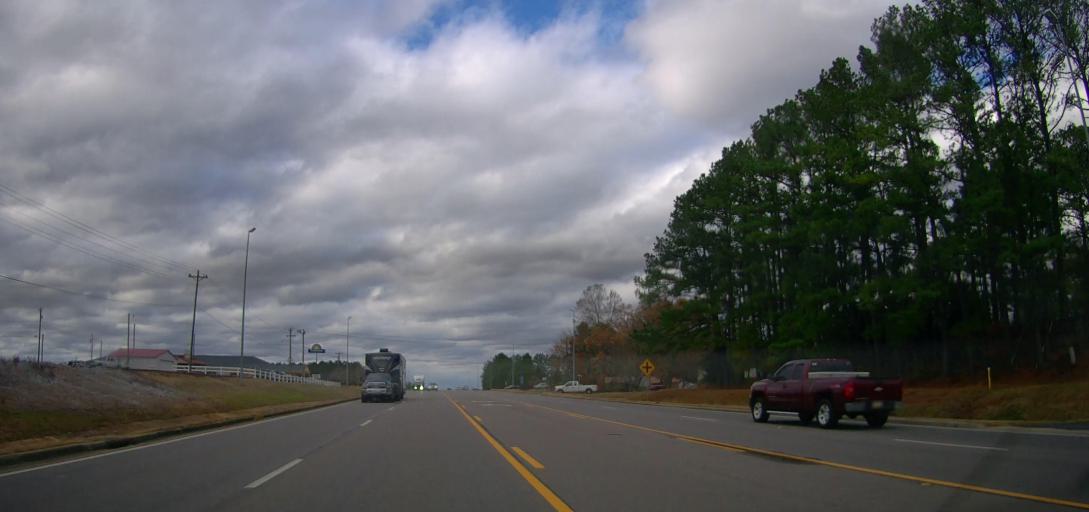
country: US
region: Alabama
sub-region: Lawrence County
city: Moulton
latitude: 34.4965
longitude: -87.2813
